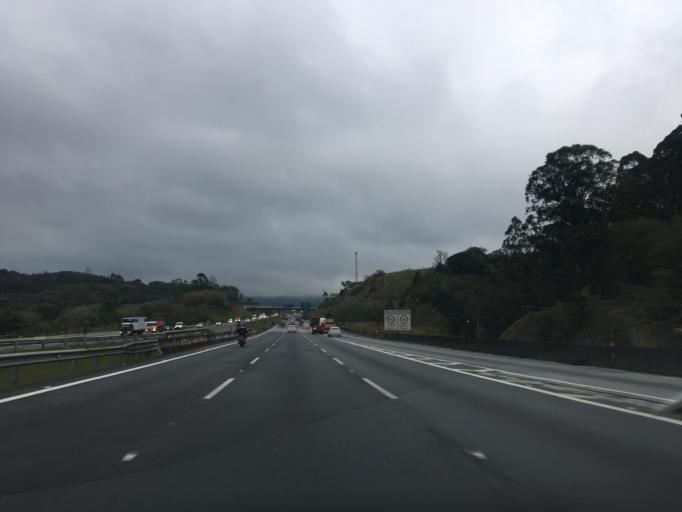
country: BR
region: Sao Paulo
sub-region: Caieiras
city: Caieiras
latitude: -23.4357
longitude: -46.7635
